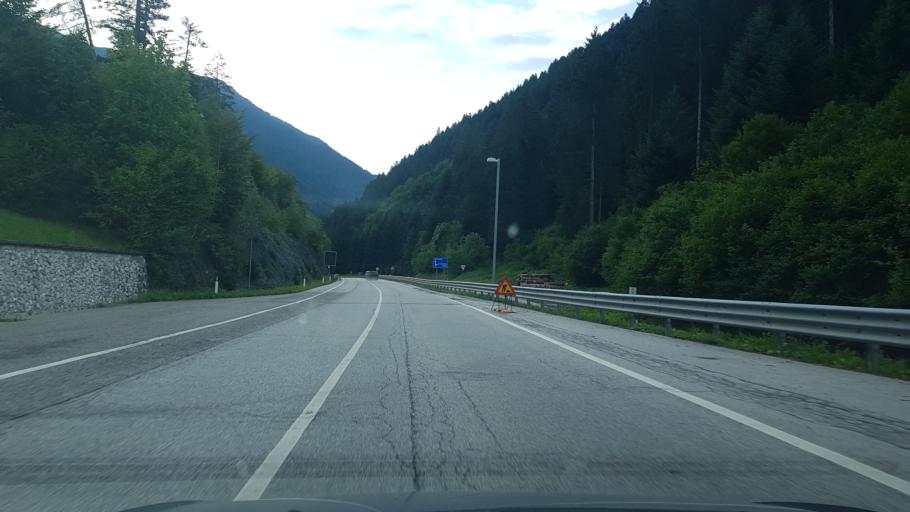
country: IT
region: Friuli Venezia Giulia
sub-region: Provincia di Udine
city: Rigolato
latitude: 46.5683
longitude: 12.8292
